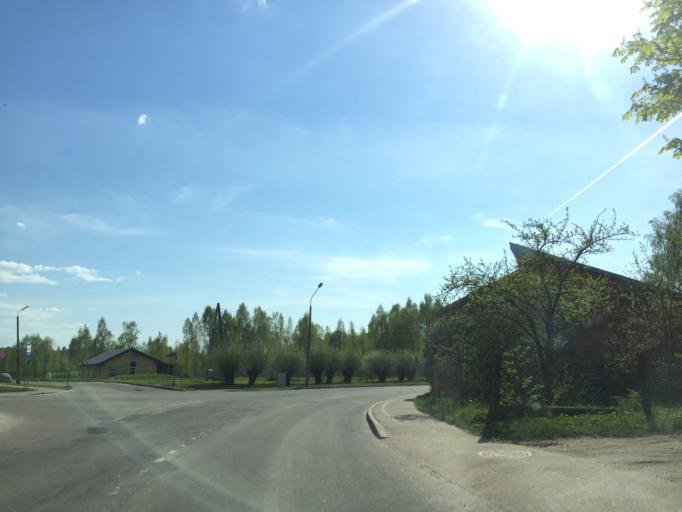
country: LV
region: Limbazu Rajons
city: Limbazi
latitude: 57.5104
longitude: 24.7058
